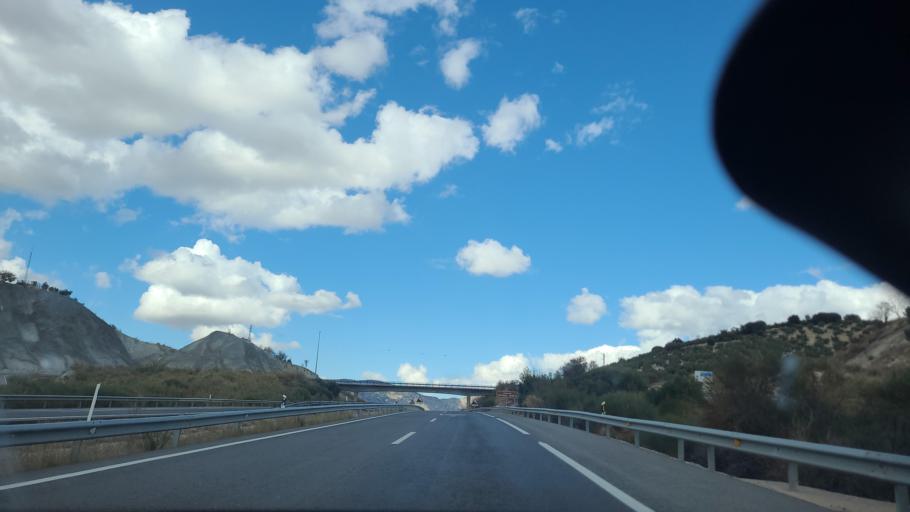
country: ES
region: Andalusia
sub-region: Provincia de Jaen
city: Noalejo
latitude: 37.5303
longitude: -3.6363
